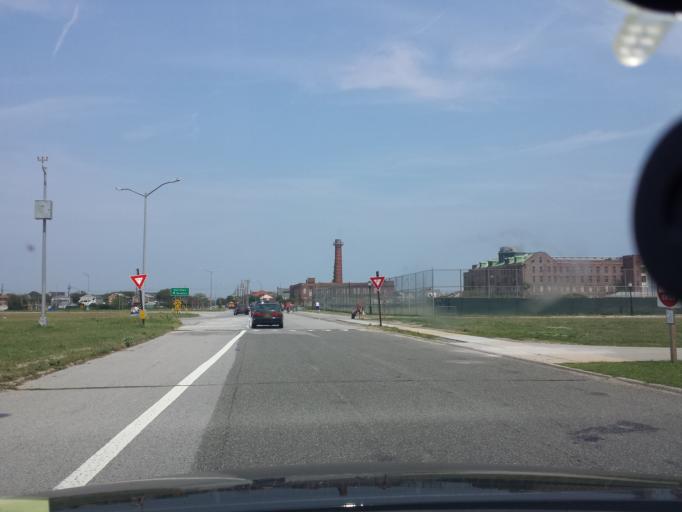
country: US
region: New York
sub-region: Kings County
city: East New York
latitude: 40.5678
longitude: -73.8679
